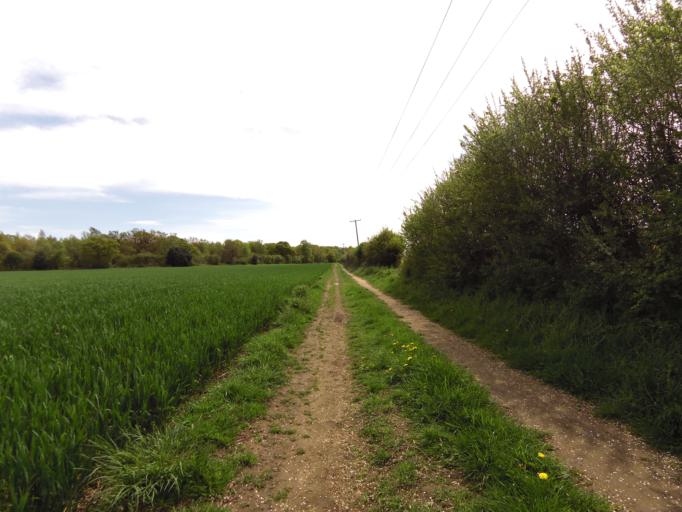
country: GB
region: England
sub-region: Suffolk
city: Ipswich
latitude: 52.0086
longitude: 1.1382
